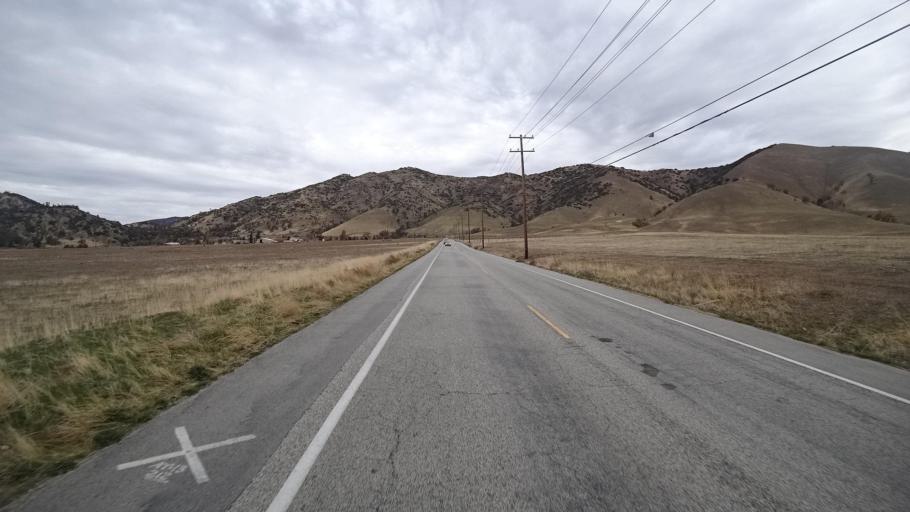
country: US
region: California
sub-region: Kern County
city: Bear Valley Springs
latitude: 35.1418
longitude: -118.5757
